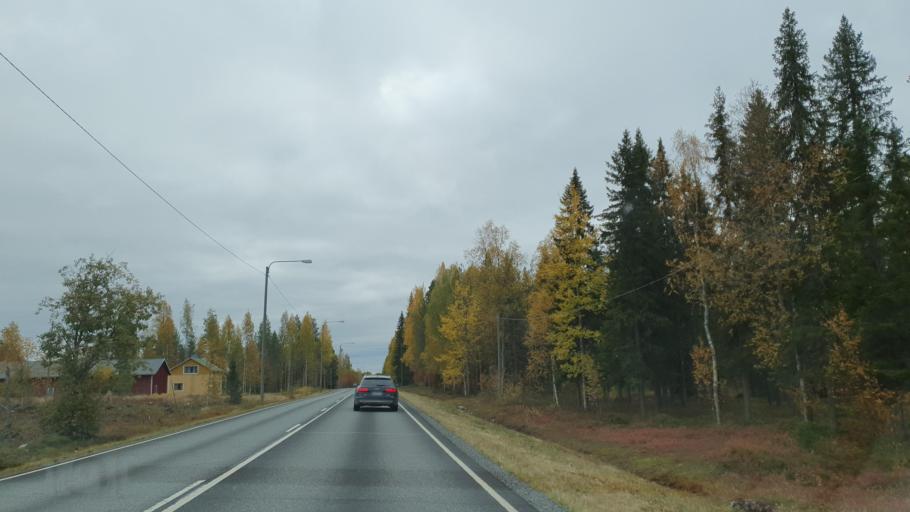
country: FI
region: Lapland
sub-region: Rovaniemi
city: Ranua
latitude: 65.7256
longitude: 26.5898
